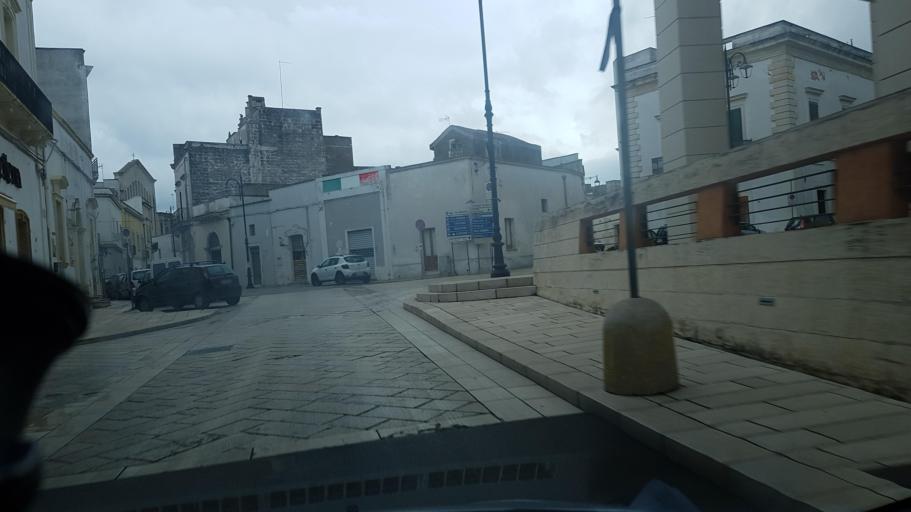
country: IT
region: Apulia
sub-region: Provincia di Lecce
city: Carmiano
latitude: 40.3464
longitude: 18.0464
